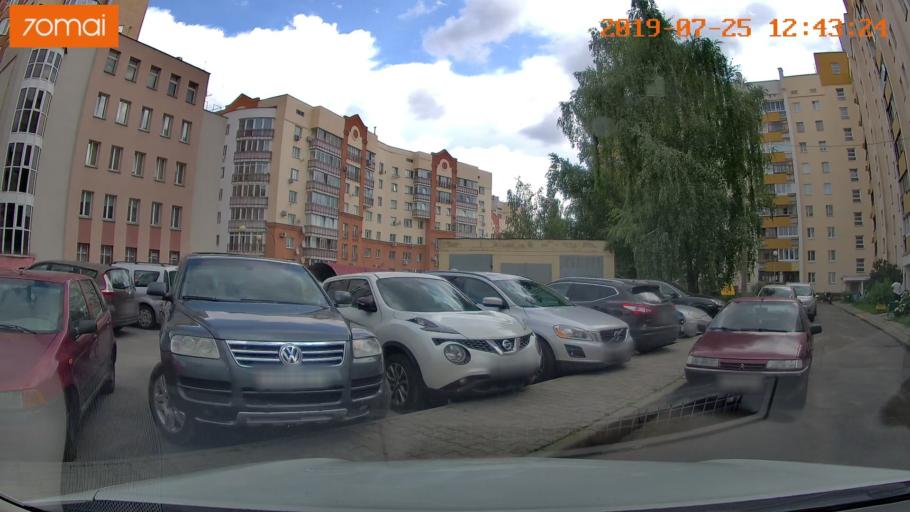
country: BY
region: Minsk
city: Minsk
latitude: 53.9130
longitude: 27.5308
